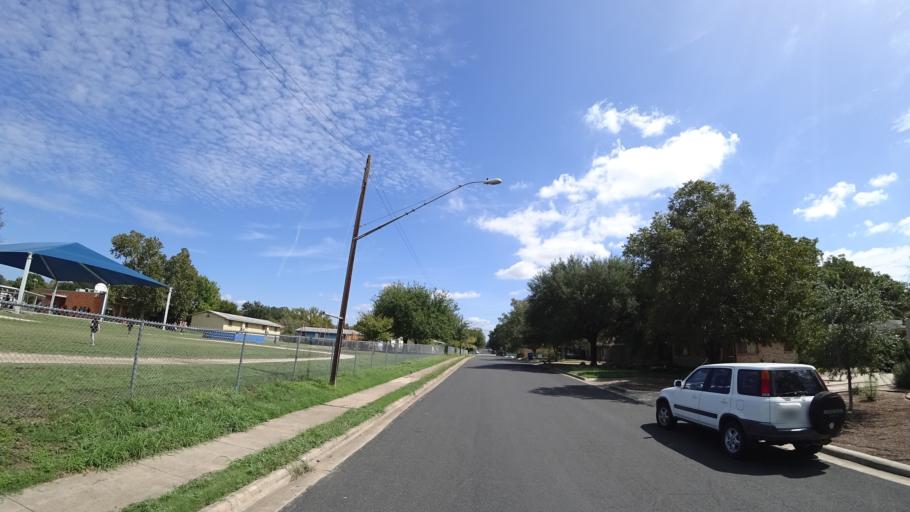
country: US
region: Texas
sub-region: Travis County
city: Austin
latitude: 30.3395
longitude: -97.7328
